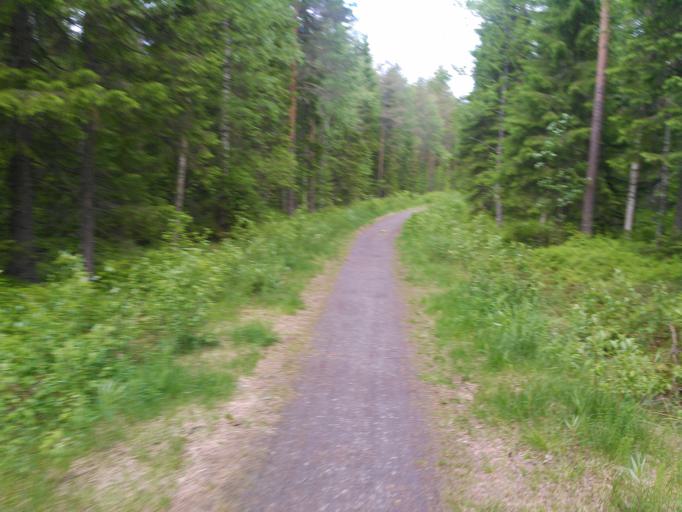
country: SE
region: Vaesterbotten
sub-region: Umea Kommun
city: Ersmark
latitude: 63.8640
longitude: 20.3338
